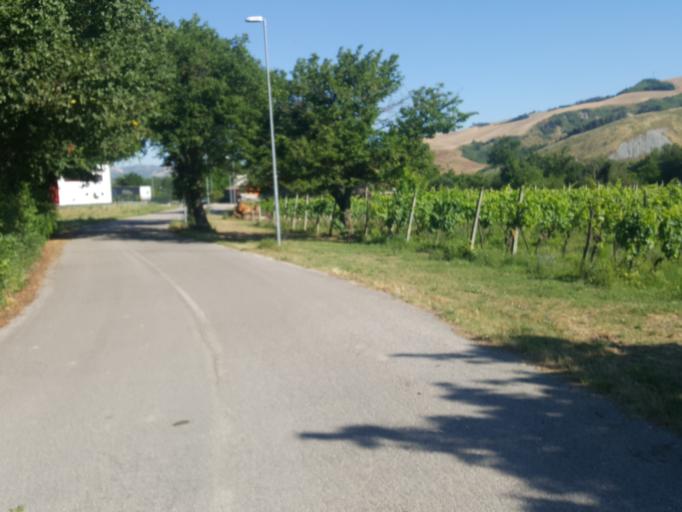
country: IT
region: The Marches
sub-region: Provincia di Pesaro e Urbino
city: Montecalvo in Foglia
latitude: 43.7844
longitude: 12.6351
